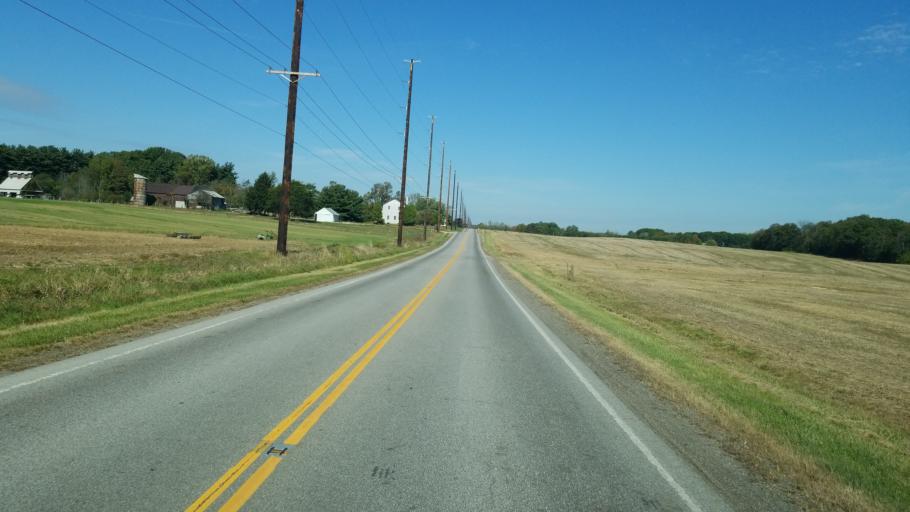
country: US
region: Ohio
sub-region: Wayne County
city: West Salem
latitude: 40.9984
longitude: -82.1129
